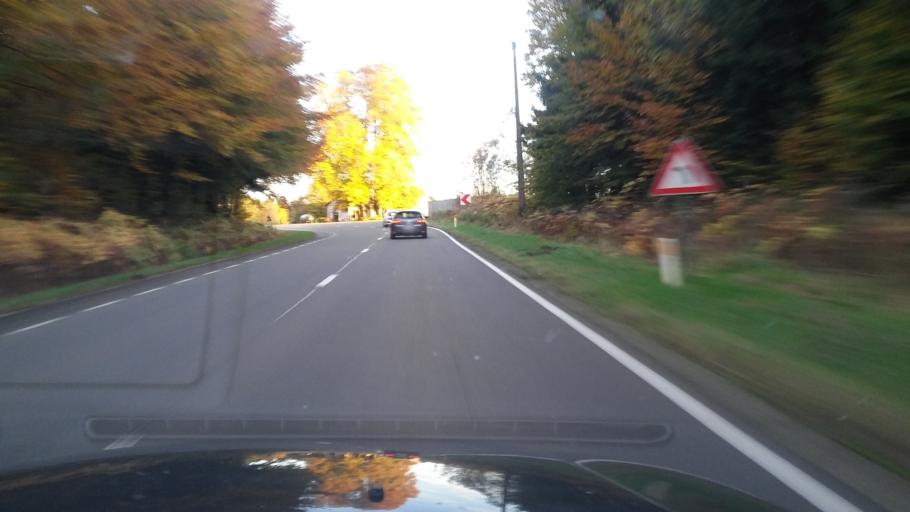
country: BE
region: Wallonia
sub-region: Province du Luxembourg
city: Herbeumont
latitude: 49.7541
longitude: 5.1613
